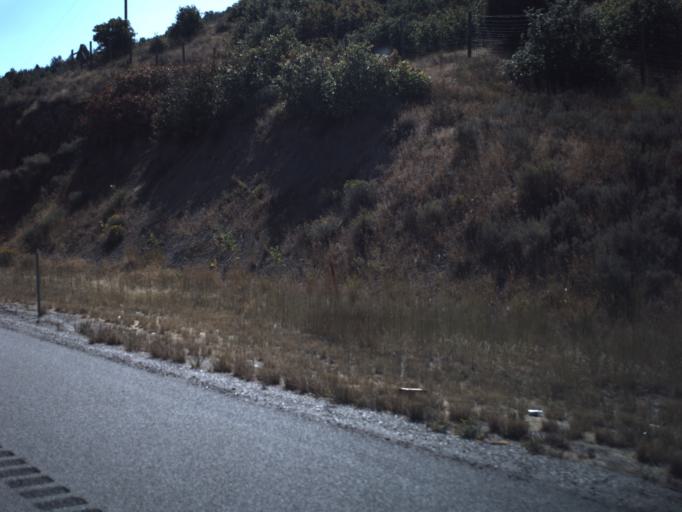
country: US
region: Utah
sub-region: Box Elder County
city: Brigham City
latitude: 41.5362
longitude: -111.9584
